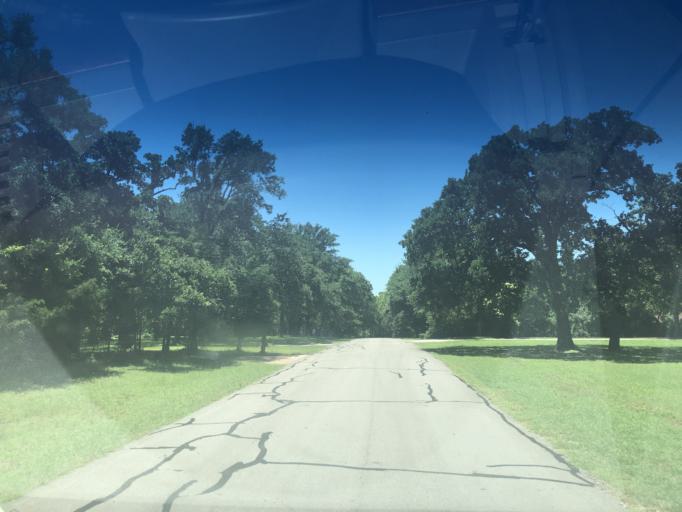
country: US
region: Texas
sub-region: Dallas County
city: Grand Prairie
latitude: 32.7784
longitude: -97.0330
